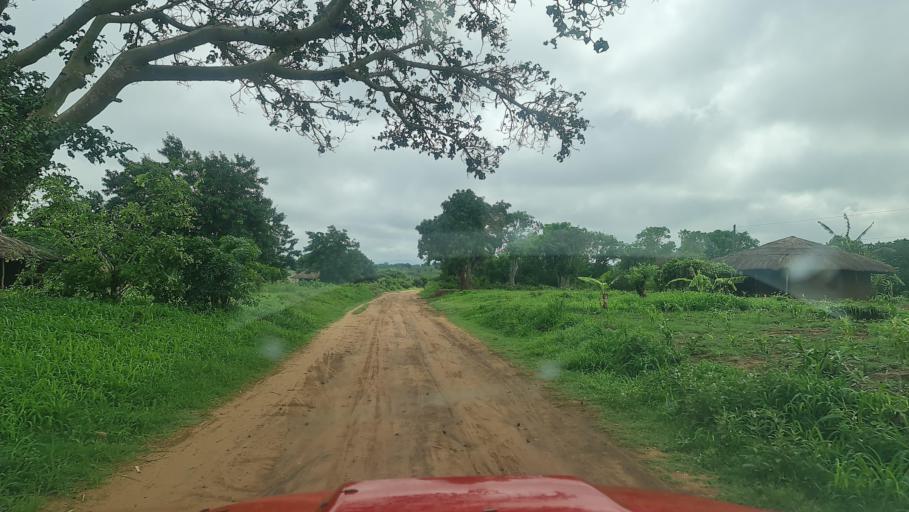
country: MW
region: Southern Region
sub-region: Nsanje District
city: Nsanje
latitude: -17.2038
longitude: 35.6851
